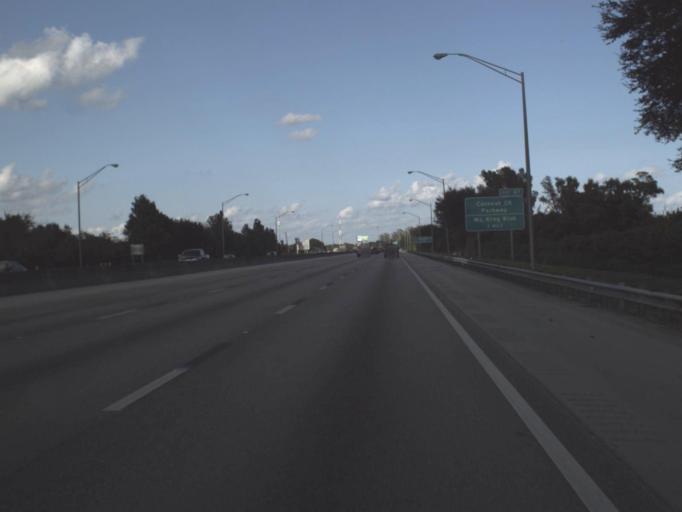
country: US
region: Florida
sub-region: Broward County
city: Coconut Creek
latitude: 26.2343
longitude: -80.1749
